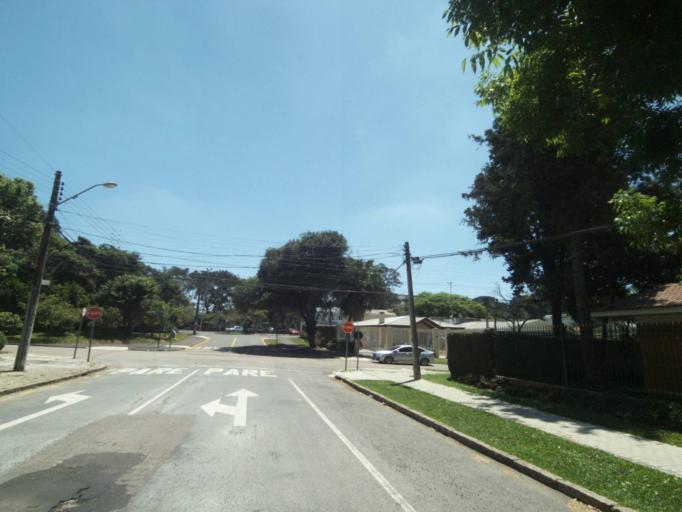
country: BR
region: Parana
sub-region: Curitiba
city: Curitiba
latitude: -25.3926
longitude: -49.2281
